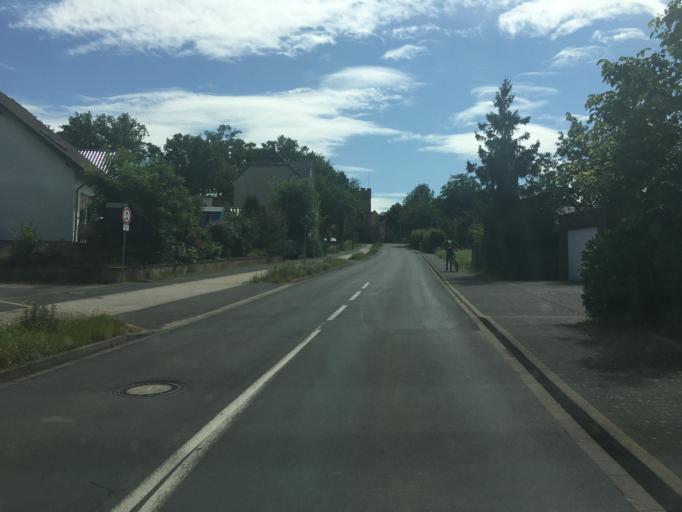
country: DE
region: North Rhine-Westphalia
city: Zulpich
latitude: 50.6958
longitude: 6.6463
